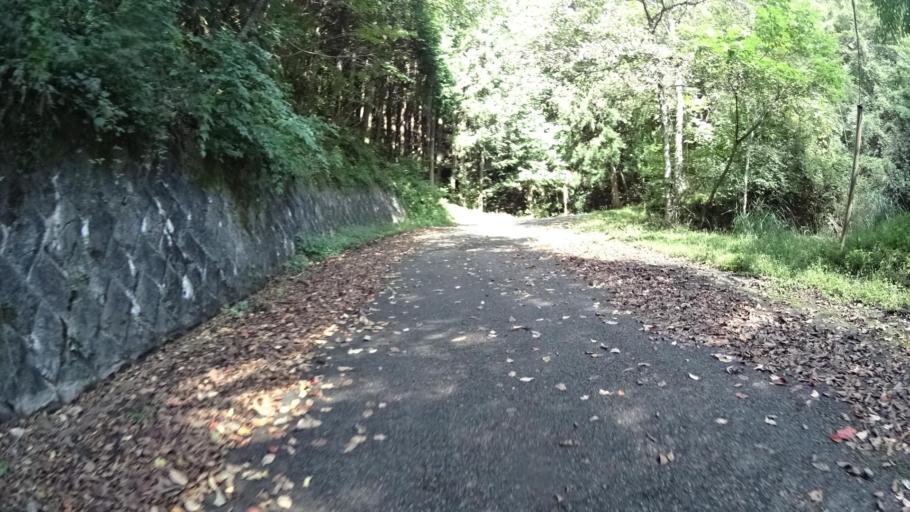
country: JP
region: Yamanashi
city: Uenohara
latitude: 35.7455
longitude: 139.0586
